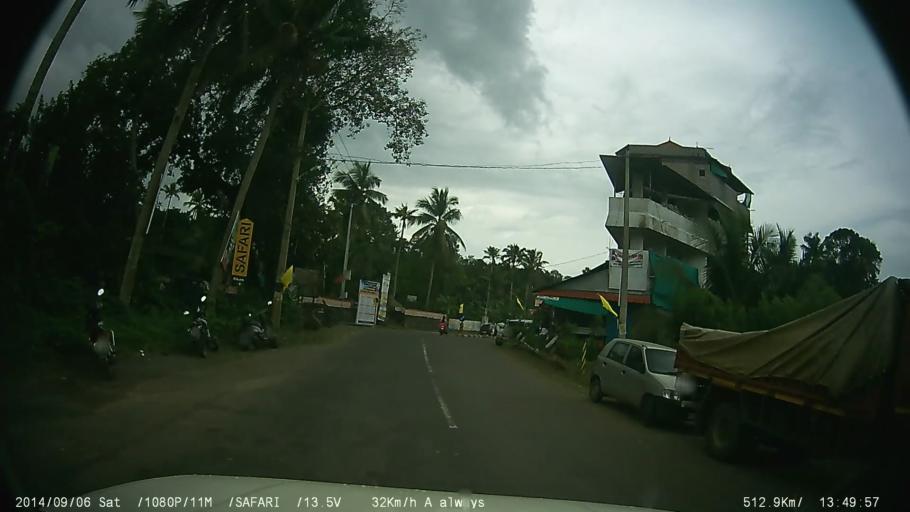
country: IN
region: Kerala
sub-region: Kottayam
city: Palackattumala
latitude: 9.7630
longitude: 76.5669
